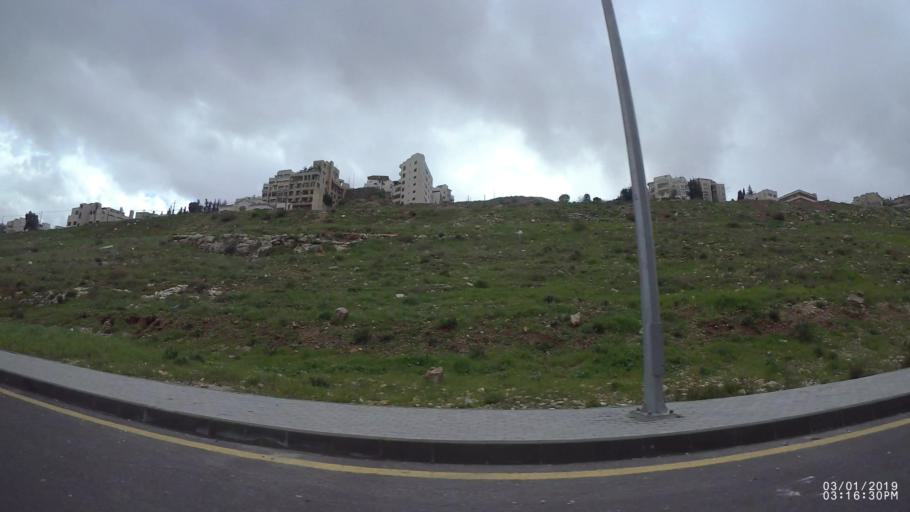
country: JO
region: Amman
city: Amman
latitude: 31.9475
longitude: 35.9038
